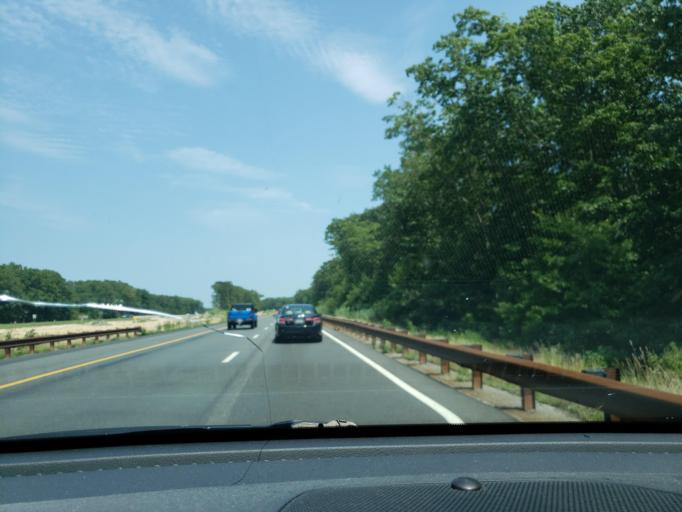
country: US
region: New Jersey
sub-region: Atlantic County
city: Linwood
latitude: 39.3558
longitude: -74.5931
